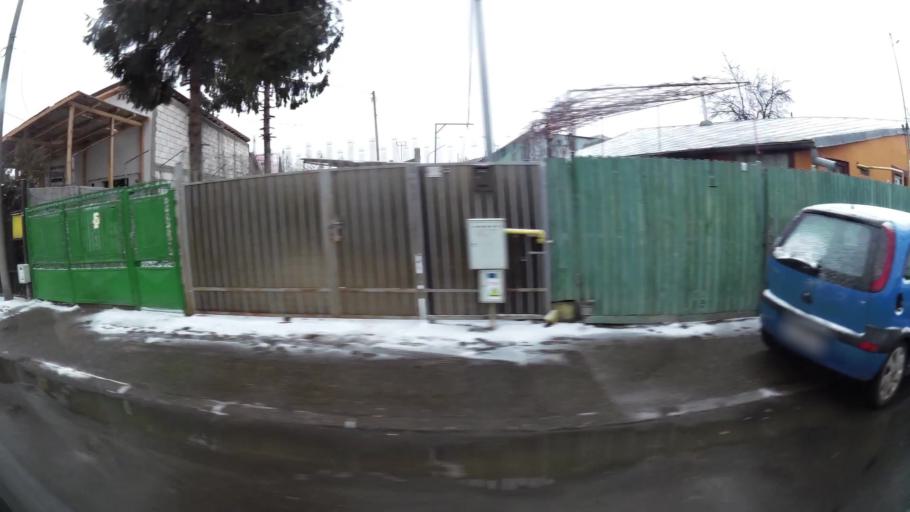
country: RO
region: Prahova
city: Ploiesti
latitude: 44.9325
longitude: 26.0484
